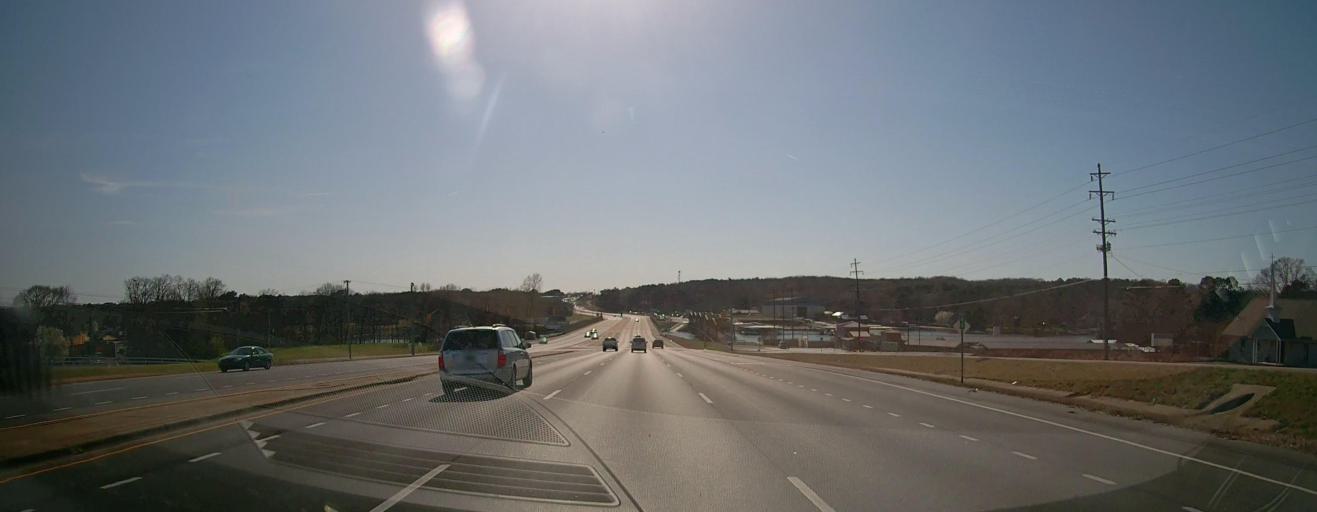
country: US
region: Alabama
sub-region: Lauderdale County
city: Killen
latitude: 34.8526
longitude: -87.5651
